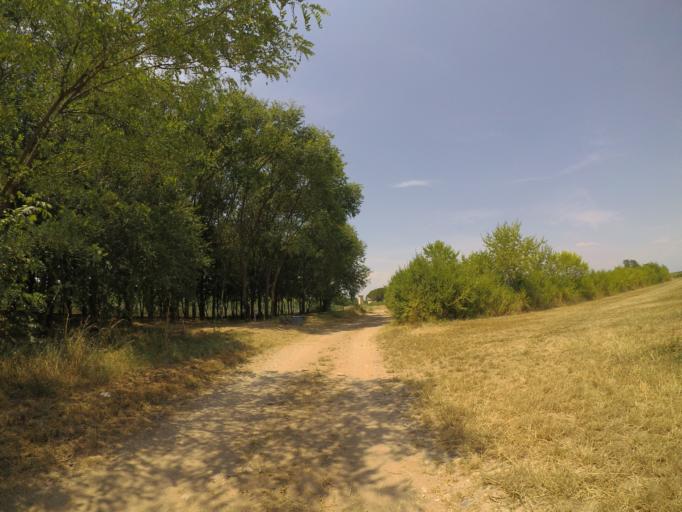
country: IT
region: Friuli Venezia Giulia
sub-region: Provincia di Udine
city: Bertiolo
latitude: 45.9521
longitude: 13.0329
